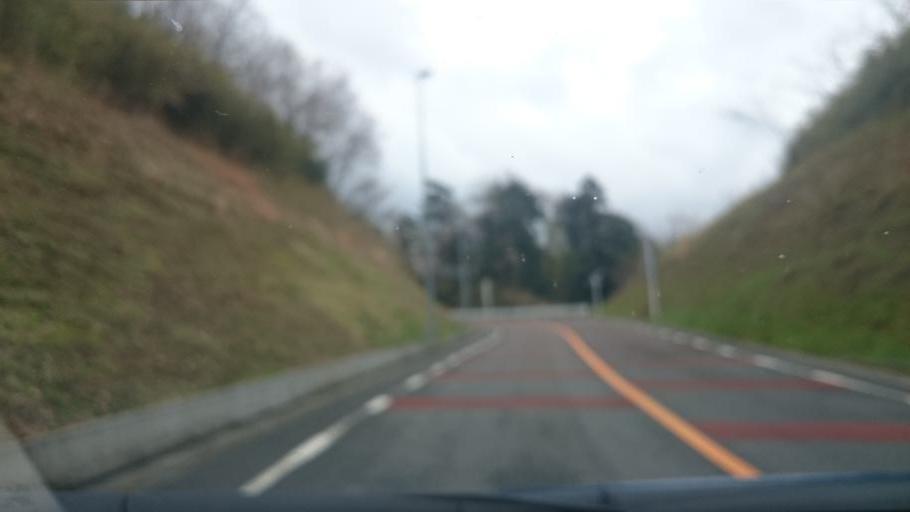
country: JP
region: Saitama
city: Yorii
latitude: 36.1129
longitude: 139.1724
